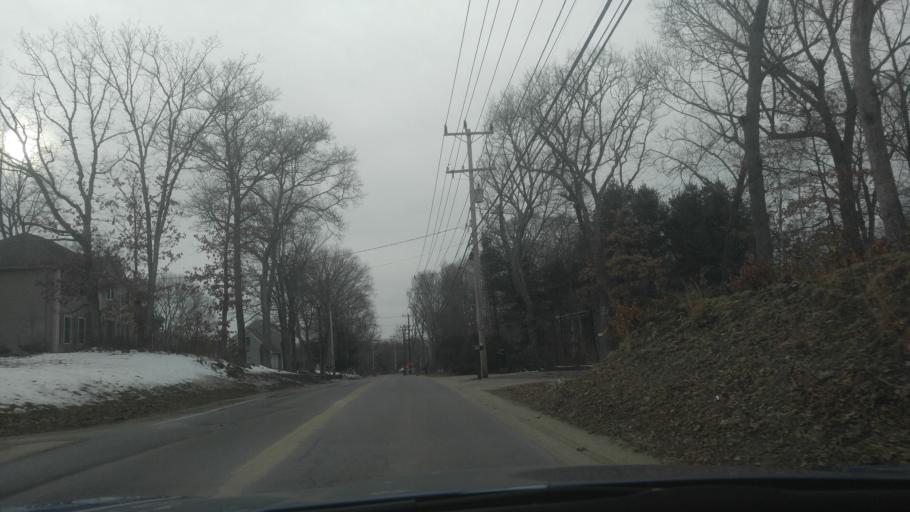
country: US
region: Rhode Island
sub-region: Kent County
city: West Warwick
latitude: 41.6734
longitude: -71.5155
